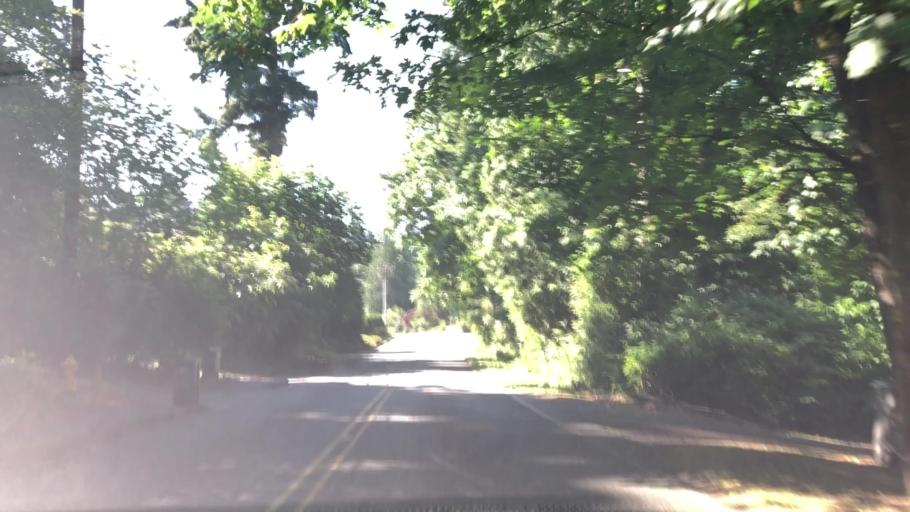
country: US
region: Washington
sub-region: Snohomish County
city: Alderwood Manor
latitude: 47.8194
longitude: -122.2524
